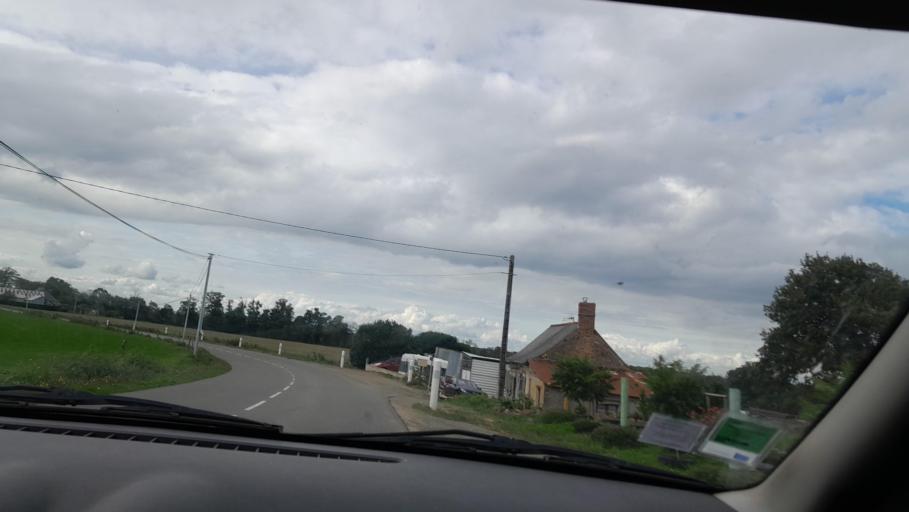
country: FR
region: Brittany
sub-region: Departement d'Ille-et-Vilaine
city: Argentre-du-Plessis
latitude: 48.0503
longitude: -1.0948
